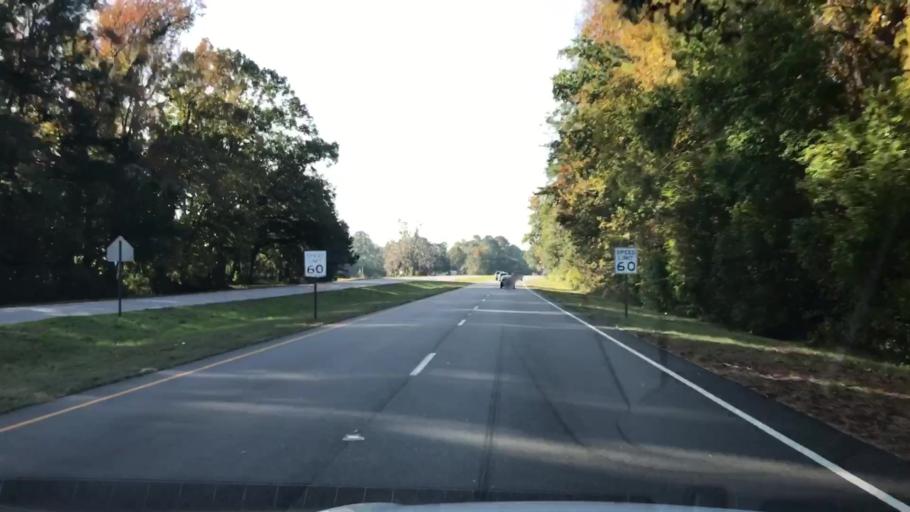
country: US
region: South Carolina
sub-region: Beaufort County
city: Laurel Bay
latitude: 32.5290
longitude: -80.7482
